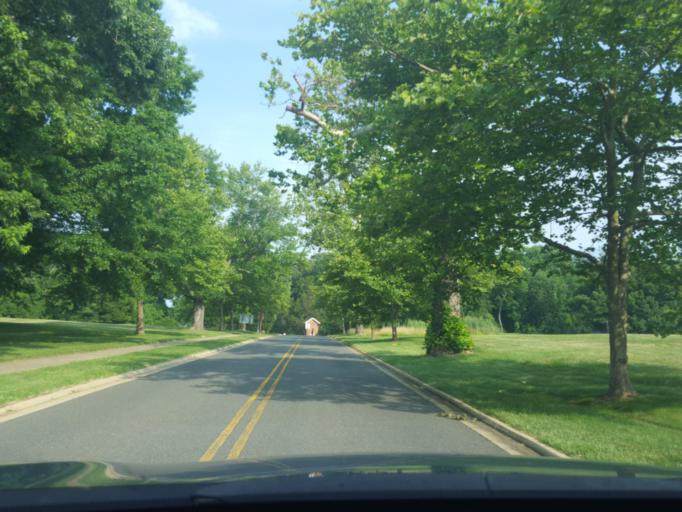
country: US
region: Maryland
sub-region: Prince George's County
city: Fort Washington
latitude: 38.7132
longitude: -77.0258
